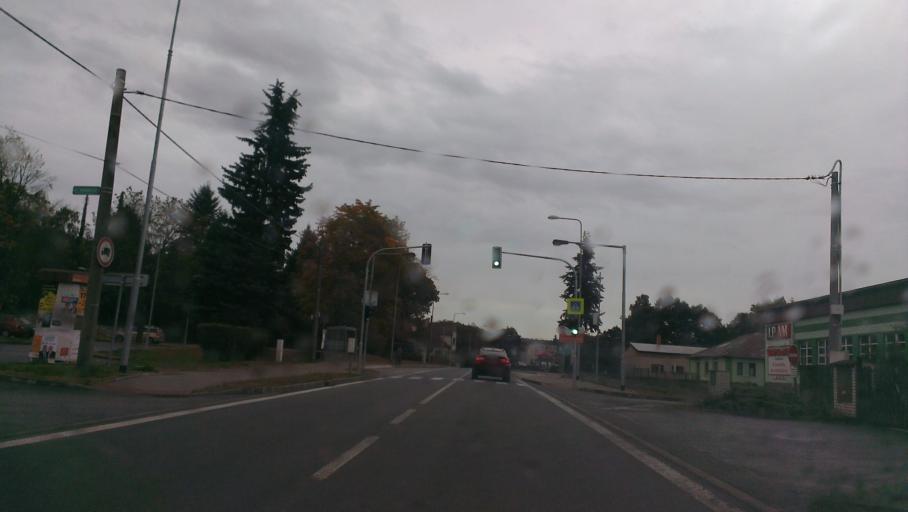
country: CZ
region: Vysocina
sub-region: Okres Zd'ar nad Sazavou
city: Velke Mezirici
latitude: 49.3482
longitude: 16.0328
